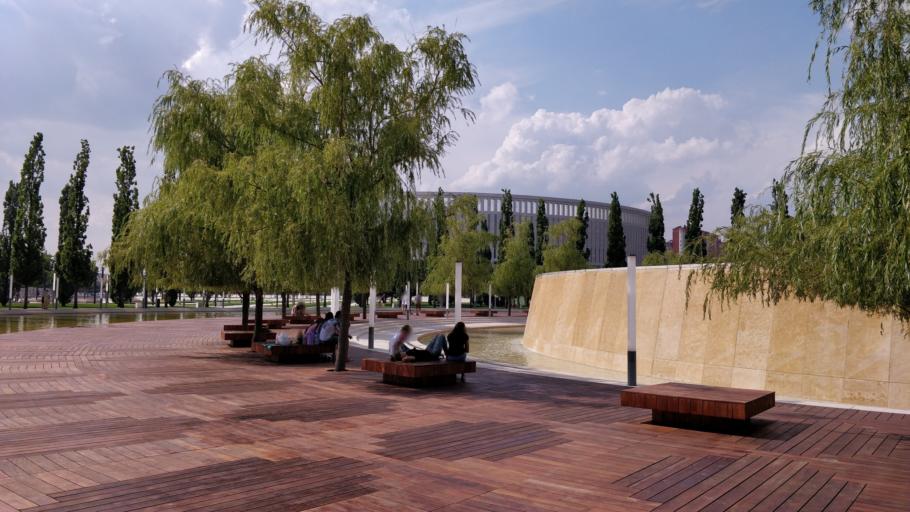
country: RU
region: Krasnodarskiy
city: Krasnodar
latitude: 45.0415
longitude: 39.0320
